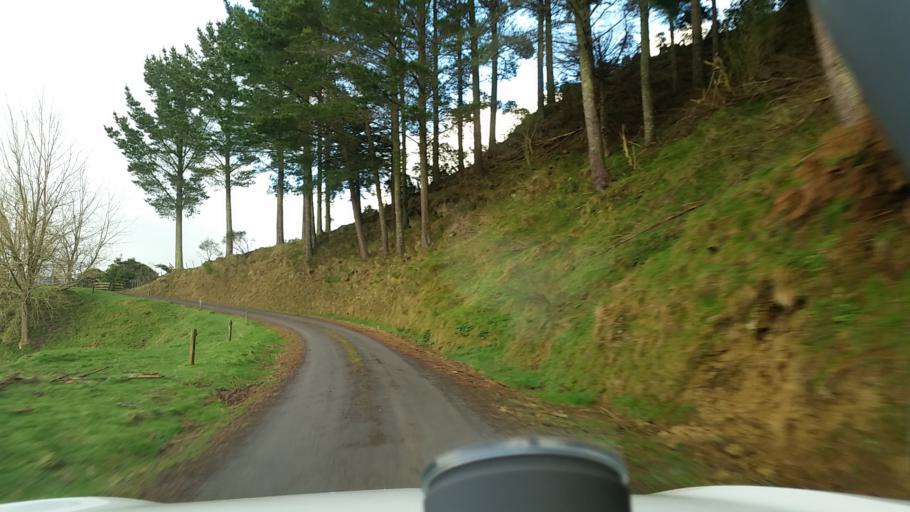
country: NZ
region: Taranaki
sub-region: South Taranaki District
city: Eltham
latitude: -39.4372
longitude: 174.4491
